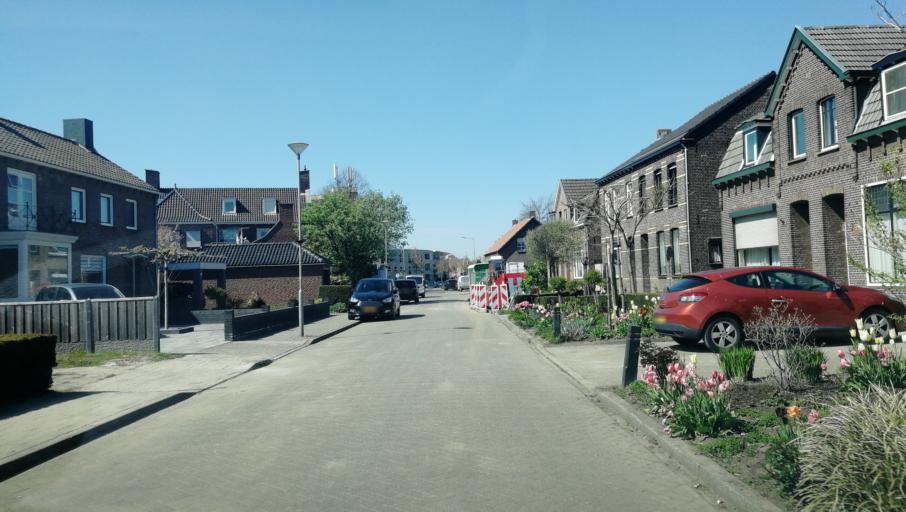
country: NL
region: Limburg
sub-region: Gemeente Venlo
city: Tegelen
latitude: 51.3405
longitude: 6.1437
